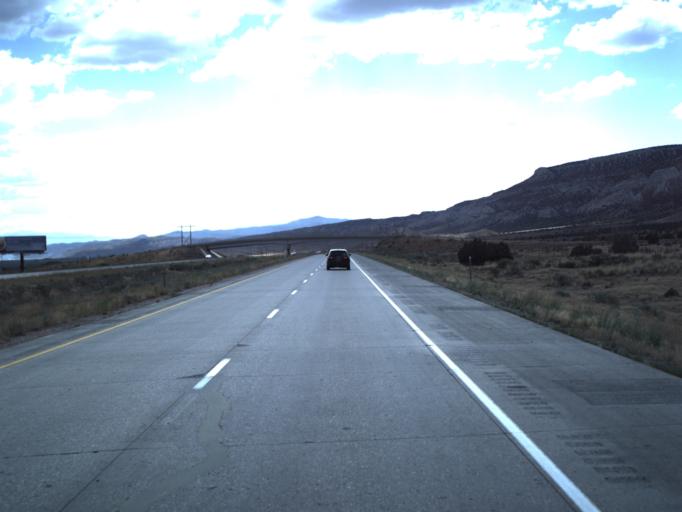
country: US
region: Utah
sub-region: Sevier County
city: Aurora
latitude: 38.8504
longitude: -112.0033
